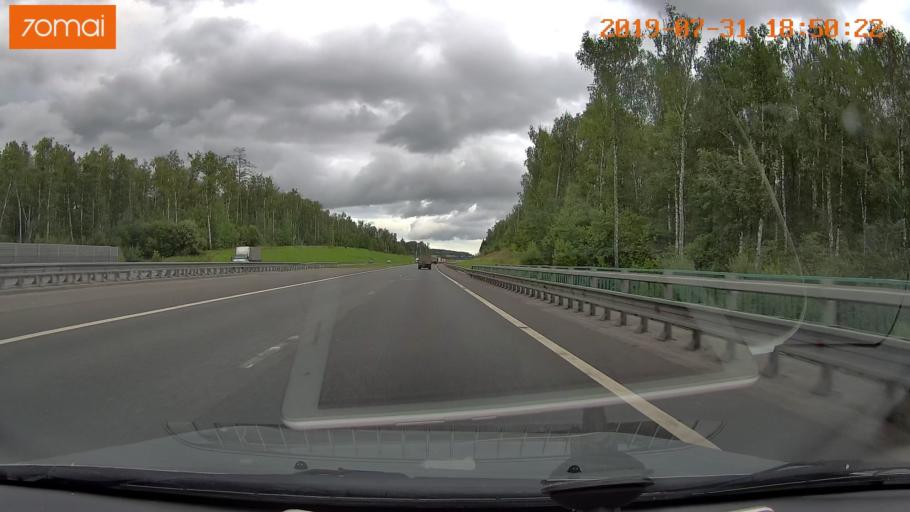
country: RU
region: Moskovskaya
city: Troitskoye
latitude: 55.2291
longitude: 38.5804
